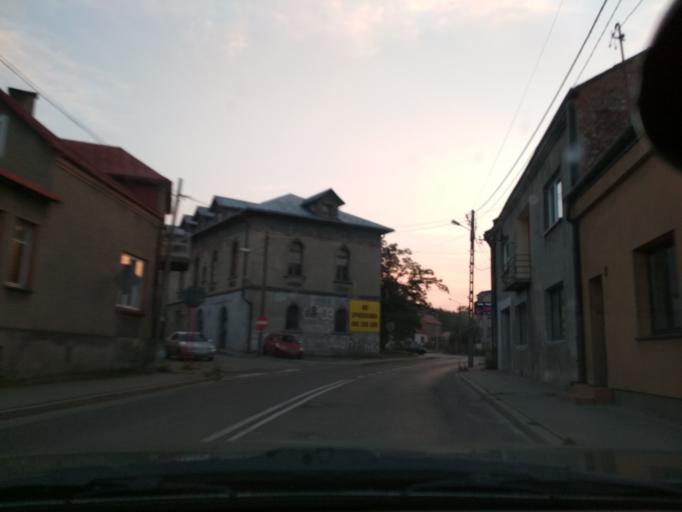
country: PL
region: Silesian Voivodeship
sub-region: Powiat zawiercianski
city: Pilica
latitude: 50.4695
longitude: 19.6580
